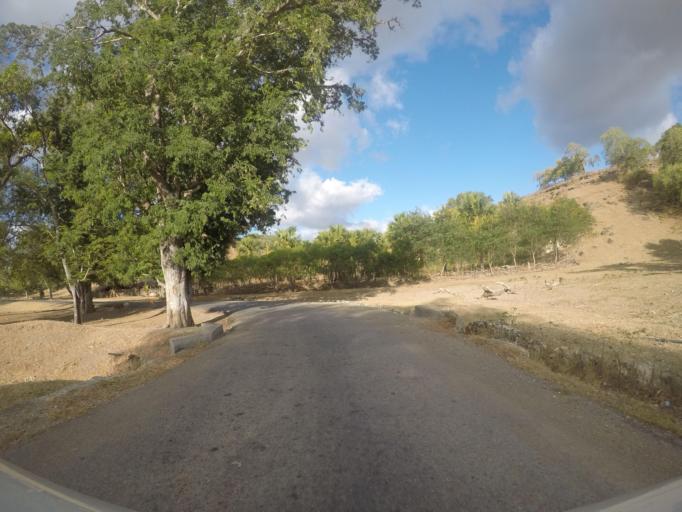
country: TL
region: Lautem
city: Lospalos
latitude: -8.4086
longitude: 126.8286
